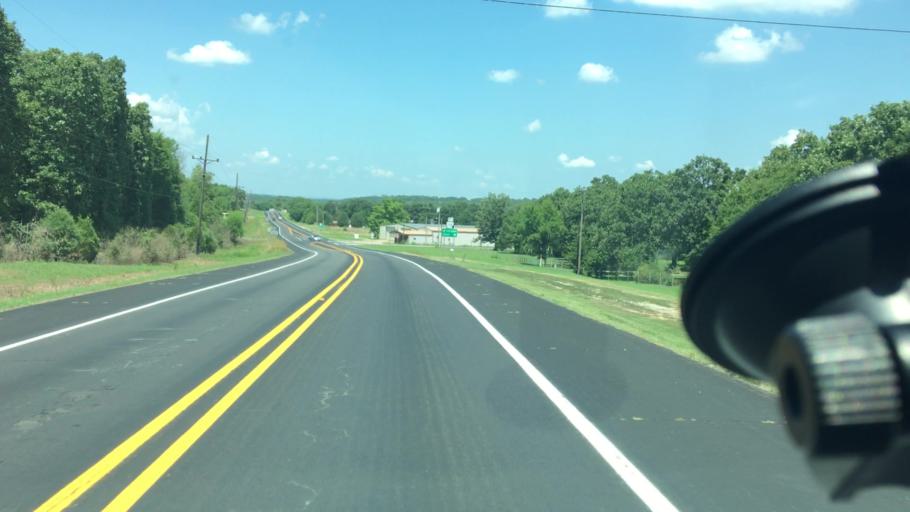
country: US
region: Arkansas
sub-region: Sebastian County
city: Lavaca
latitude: 35.3012
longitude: -94.1605
